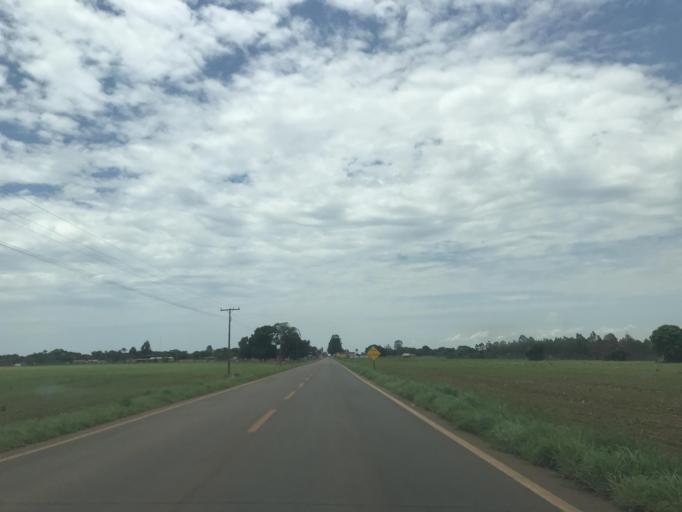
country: BR
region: Goias
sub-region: Luziania
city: Luziania
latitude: -16.3060
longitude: -48.0124
